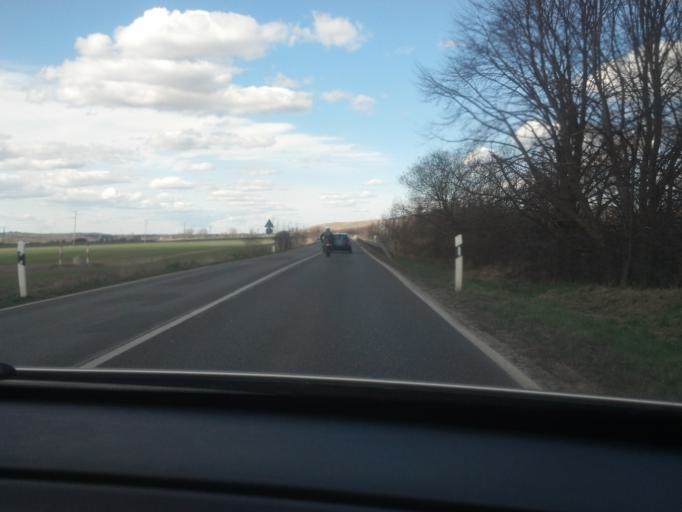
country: DE
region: Mecklenburg-Vorpommern
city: Trollenhagen
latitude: 53.6024
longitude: 13.2697
